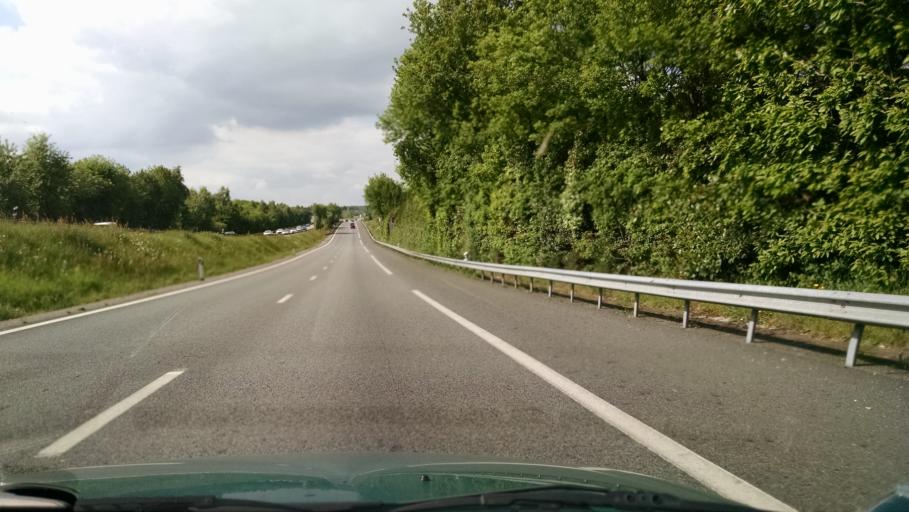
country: FR
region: Brittany
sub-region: Departement d'Ille-et-Vilaine
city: Crevin
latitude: 47.9558
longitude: -1.6820
